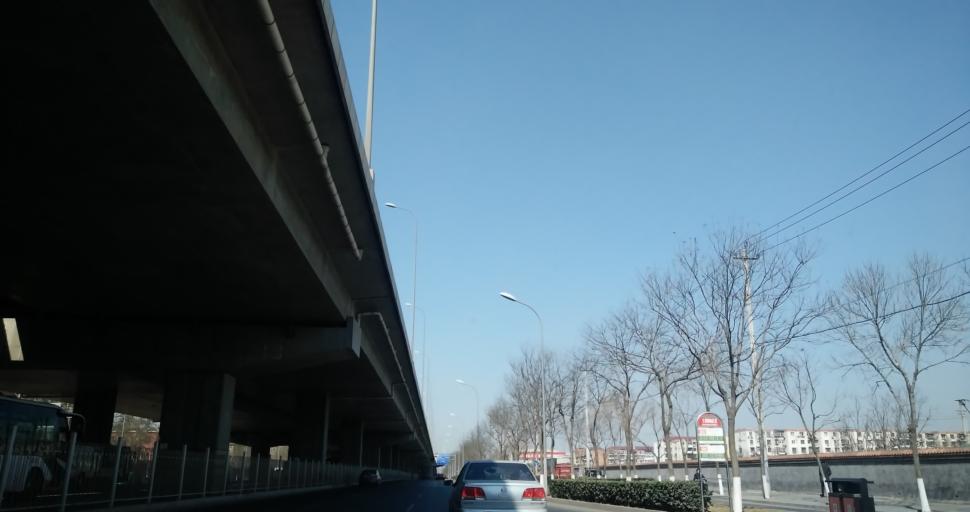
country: CN
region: Beijing
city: Jiugong
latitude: 39.7985
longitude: 116.4239
